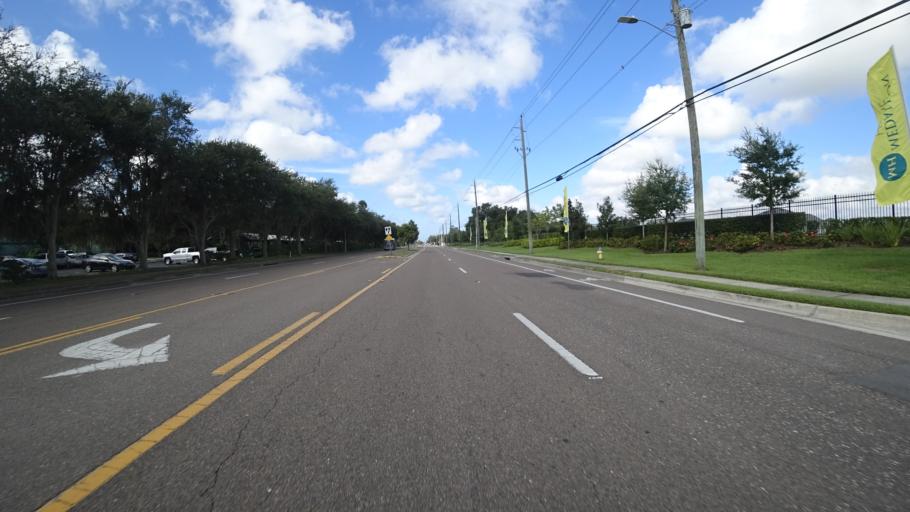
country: US
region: Florida
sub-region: Sarasota County
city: North Sarasota
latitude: 27.4035
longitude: -82.5259
